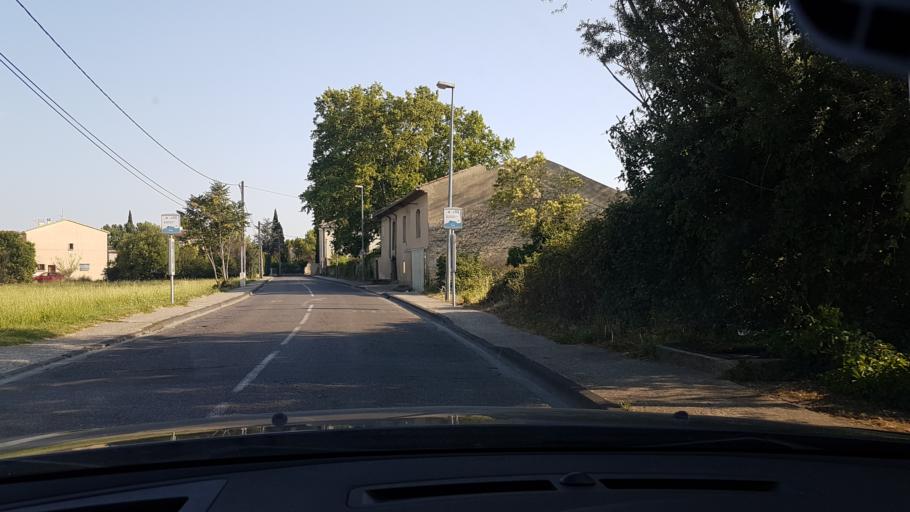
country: FR
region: Provence-Alpes-Cote d'Azur
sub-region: Departement du Vaucluse
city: Carpentras
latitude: 44.0496
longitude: 5.0532
